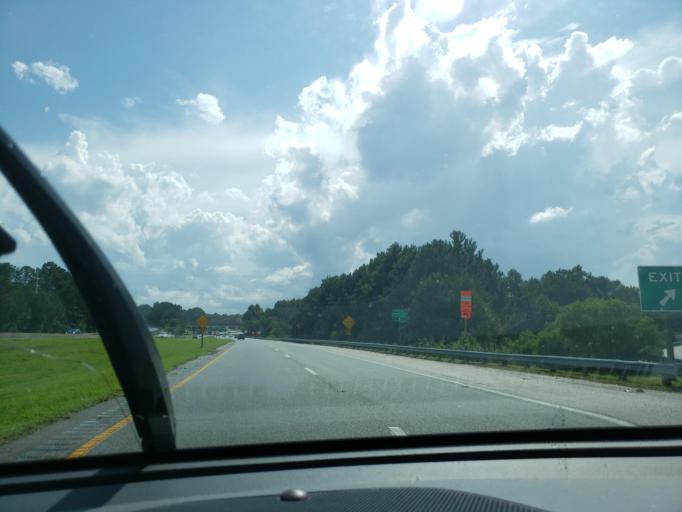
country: US
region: Virginia
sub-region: City of Suffolk
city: South Suffolk
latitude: 36.7297
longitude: -76.6298
